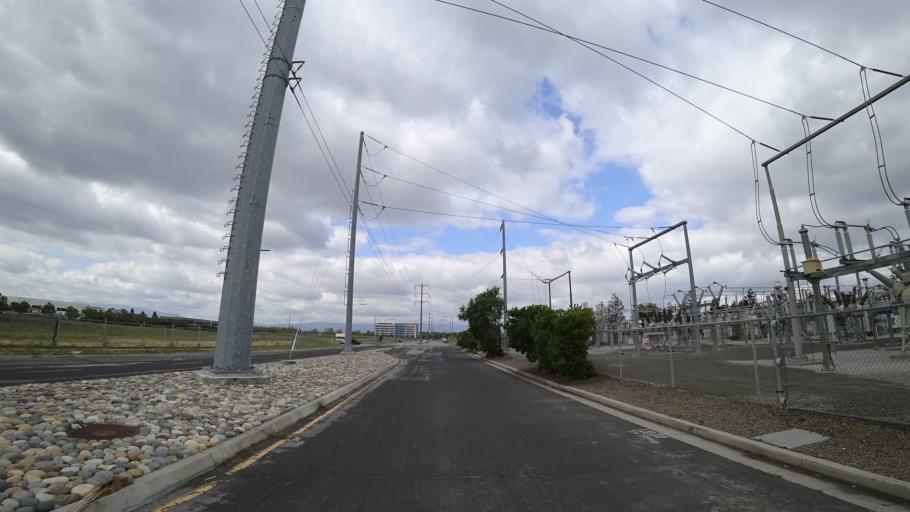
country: US
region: California
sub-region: Santa Clara County
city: Santa Clara
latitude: 37.3820
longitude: -121.9265
